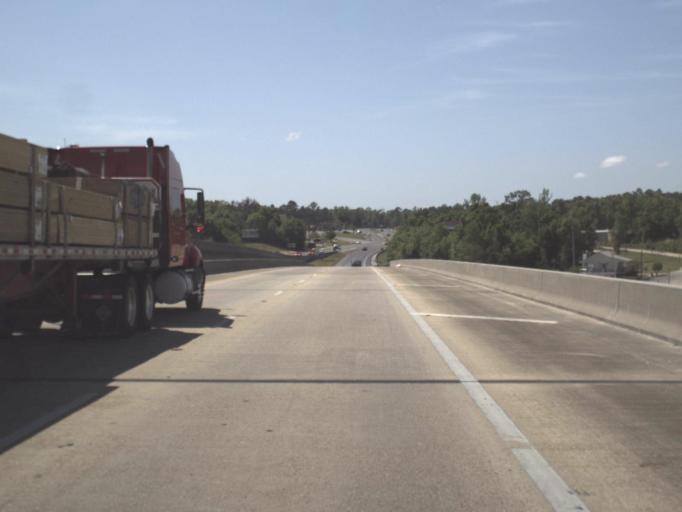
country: US
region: Florida
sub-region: Escambia County
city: Ferry Pass
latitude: 30.5478
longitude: -87.1956
